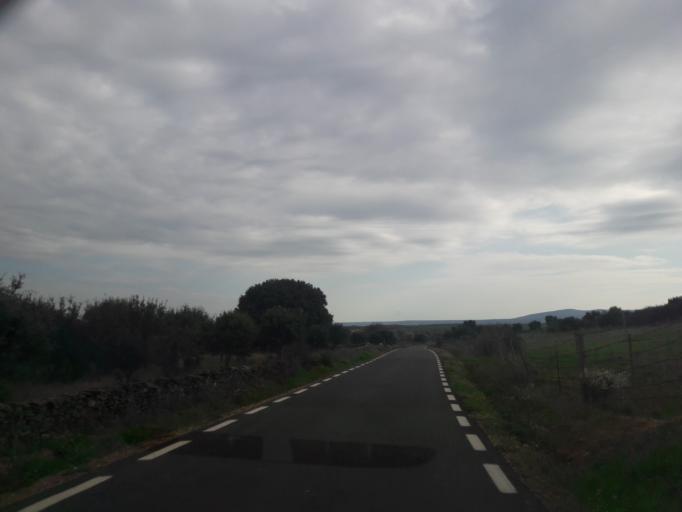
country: ES
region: Castille and Leon
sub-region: Provincia de Salamanca
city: Pastores
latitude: 40.5062
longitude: -6.5196
